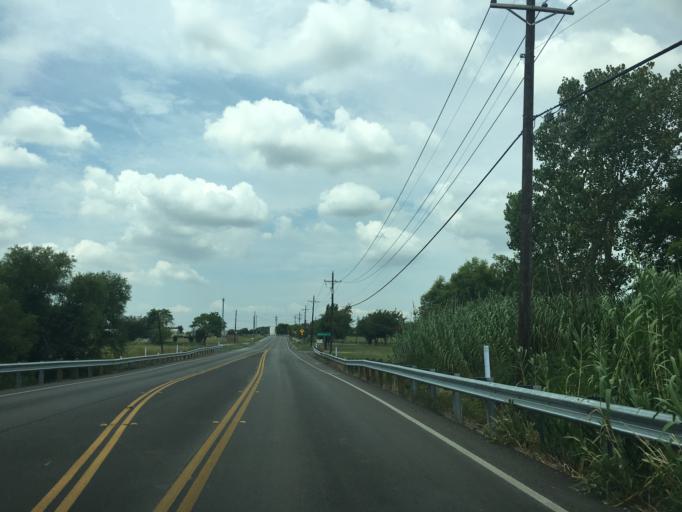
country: US
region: Texas
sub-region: Rockwall County
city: Fate
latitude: 32.9661
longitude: -96.3747
